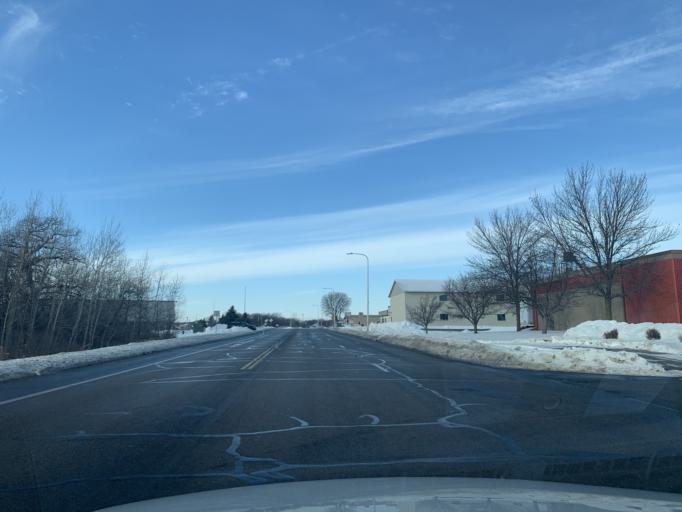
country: US
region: Minnesota
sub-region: Wright County
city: Buffalo
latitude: 45.1656
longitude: -93.8534
